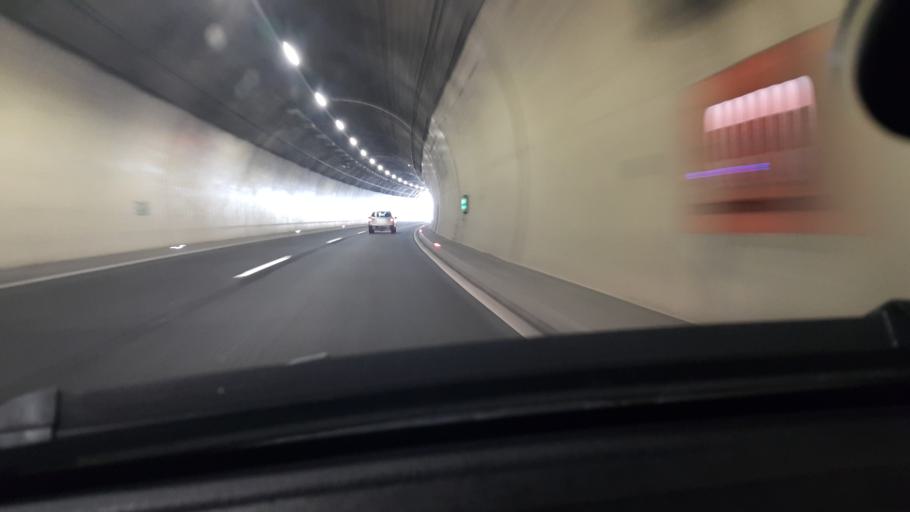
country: AT
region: Carinthia
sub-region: Politischer Bezirk Volkermarkt
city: Griffen
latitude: 46.6994
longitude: 14.7564
